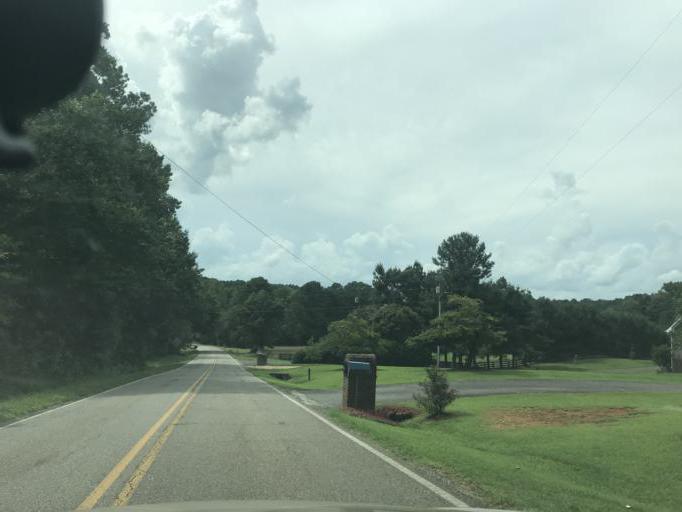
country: US
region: Georgia
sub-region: Forsyth County
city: Cumming
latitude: 34.2869
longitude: -84.2387
